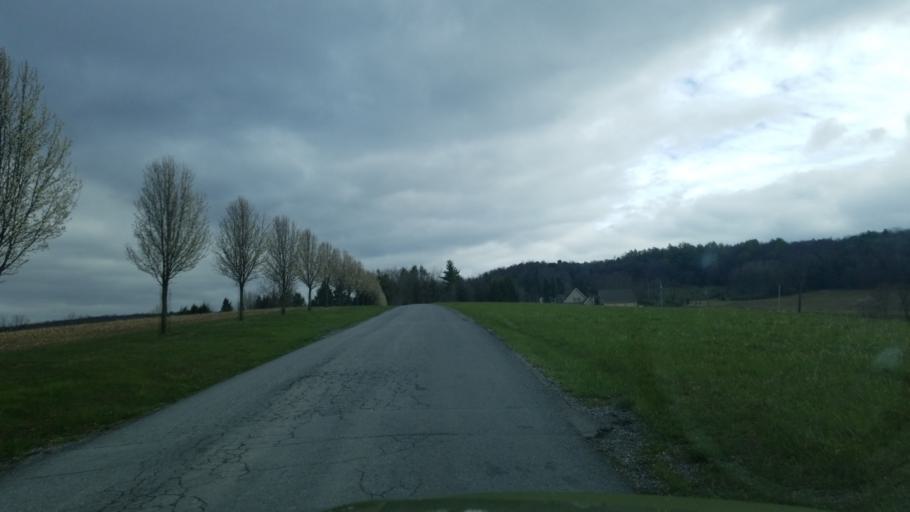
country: US
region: Pennsylvania
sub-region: Clearfield County
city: Shiloh
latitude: 41.1098
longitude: -78.3433
